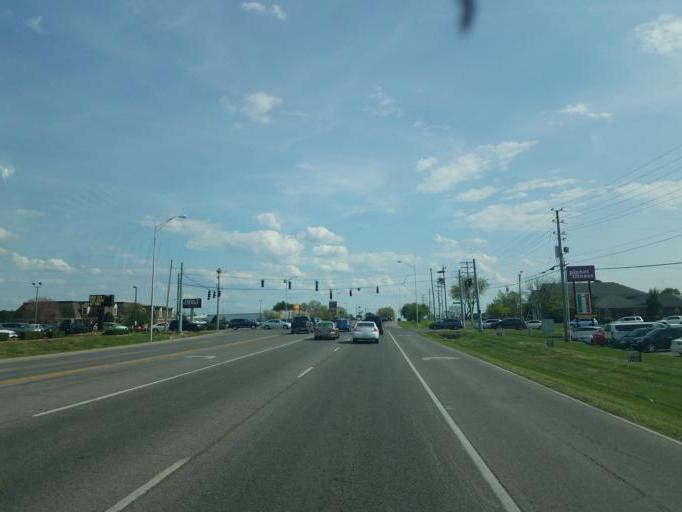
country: US
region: Kentucky
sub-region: Warren County
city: Bowling Green
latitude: 36.9668
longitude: -86.4326
